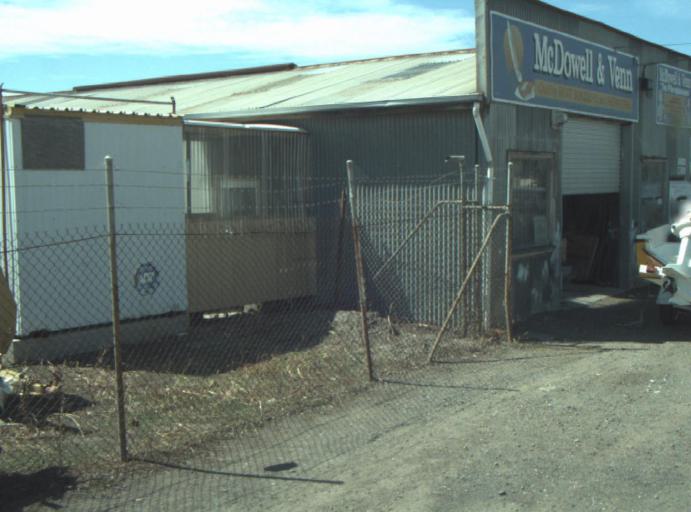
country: AU
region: Victoria
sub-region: Greater Geelong
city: East Geelong
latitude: -38.1680
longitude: 144.4087
